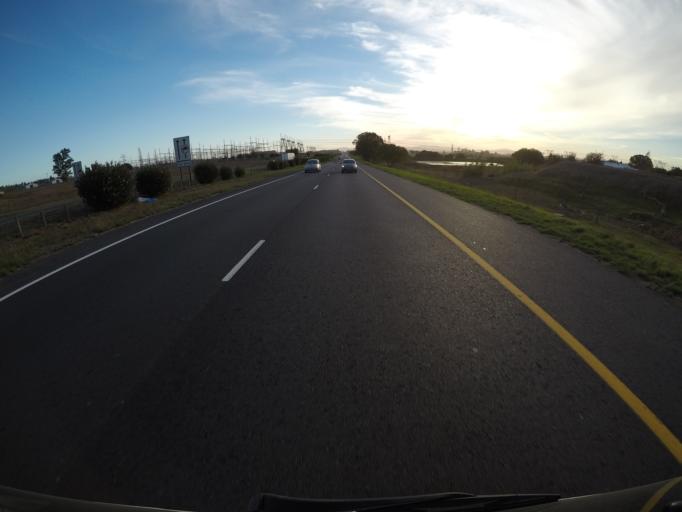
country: ZA
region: Western Cape
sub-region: City of Cape Town
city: Kraaifontein
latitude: -33.8142
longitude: 18.8114
